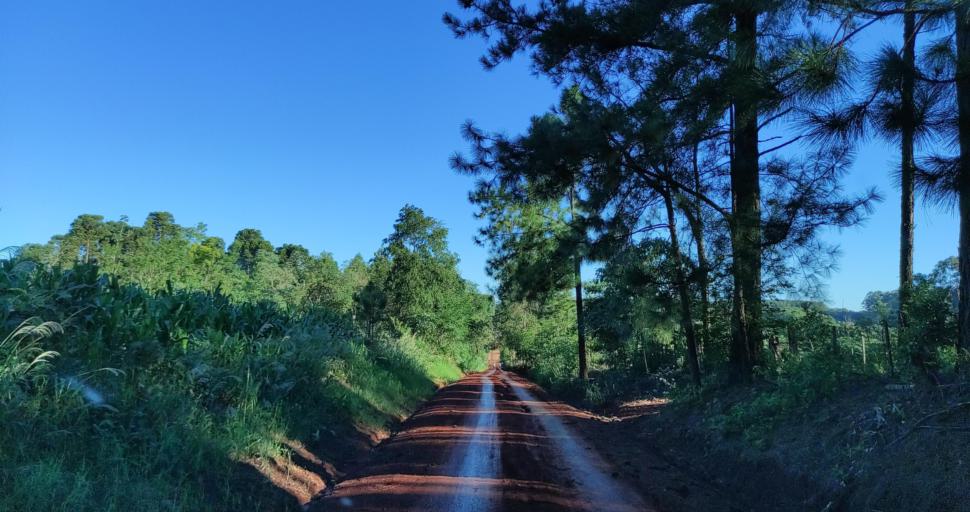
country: AR
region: Misiones
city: Puerto Rico
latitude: -26.8462
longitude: -55.0132
